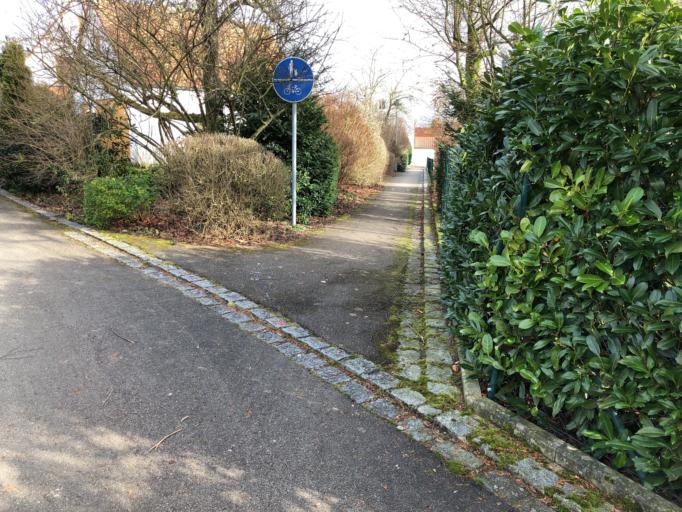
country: DE
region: Bavaria
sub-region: Swabia
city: Wertingen
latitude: 48.5586
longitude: 10.6759
